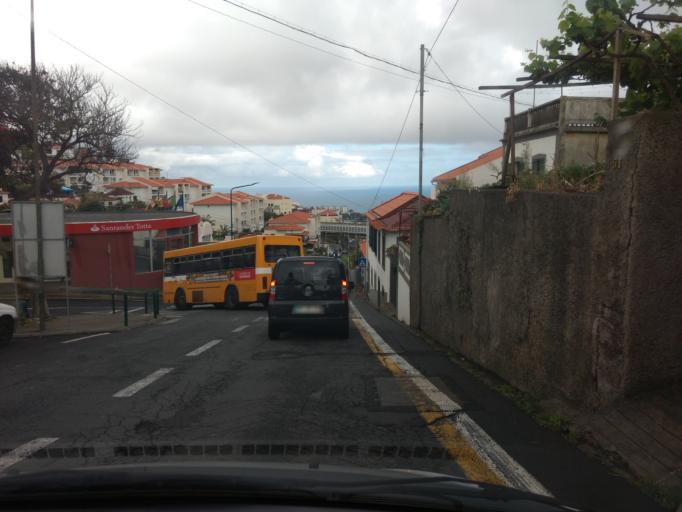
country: PT
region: Madeira
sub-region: Funchal
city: Nossa Senhora do Monte
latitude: 32.6634
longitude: -16.9293
